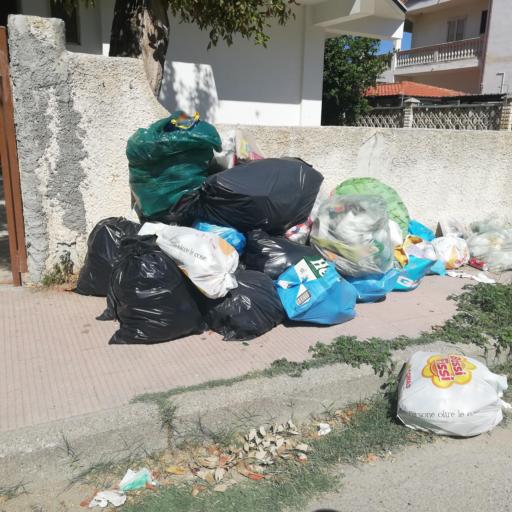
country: IT
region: Calabria
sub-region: Provincia di Cosenza
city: Caloppezzati
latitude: 39.5466
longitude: 16.8535
